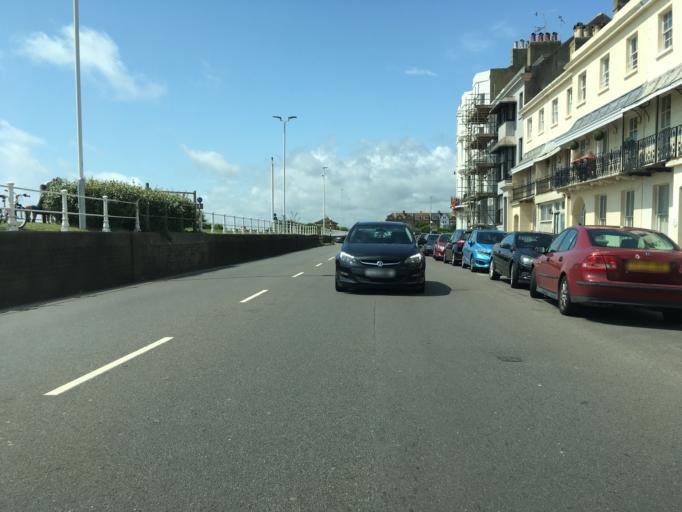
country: GB
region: England
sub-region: East Sussex
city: Saint Leonards-on-Sea
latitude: 50.8506
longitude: 0.5454
